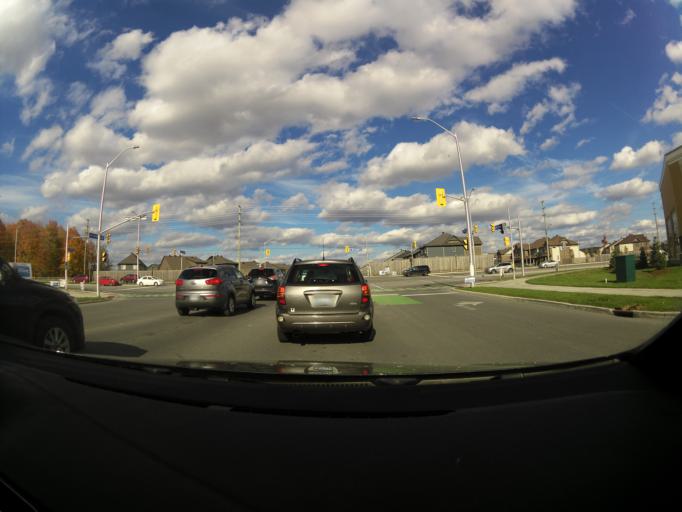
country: CA
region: Ontario
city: Bells Corners
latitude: 45.2714
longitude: -75.7841
